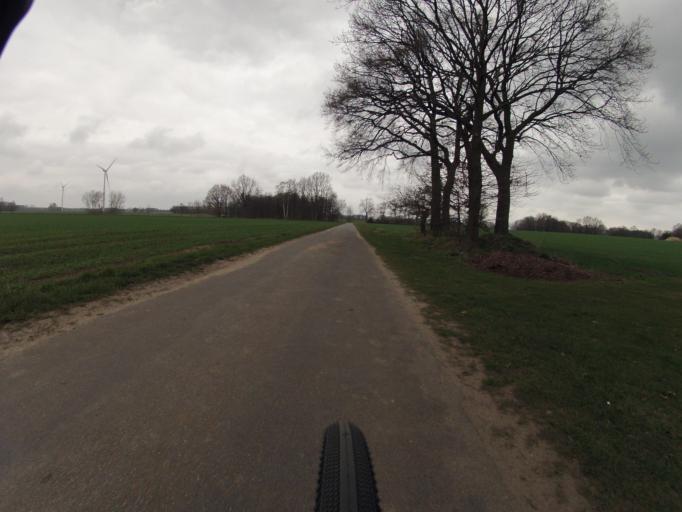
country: DE
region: North Rhine-Westphalia
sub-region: Regierungsbezirk Munster
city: Mettingen
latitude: 52.3402
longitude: 7.8128
